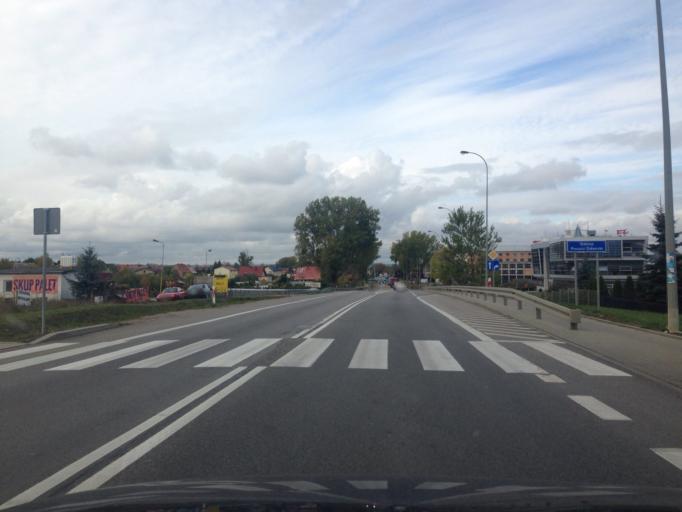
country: PL
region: Pomeranian Voivodeship
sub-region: Powiat gdanski
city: Legowo
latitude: 54.2145
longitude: 18.6559
